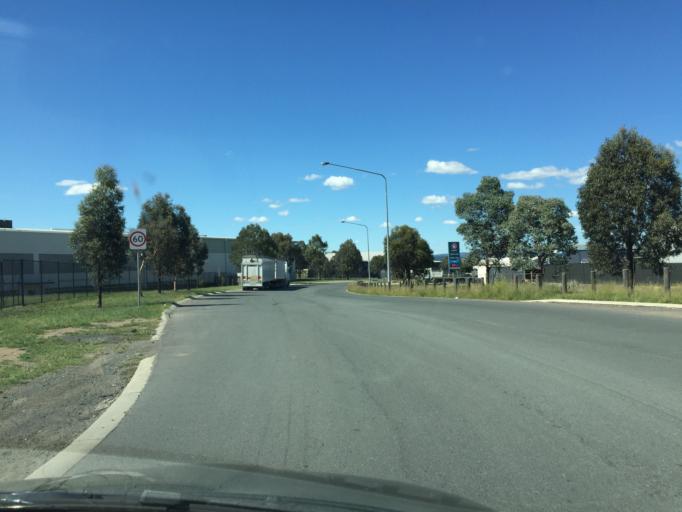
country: AU
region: Australian Capital Territory
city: Macarthur
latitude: -35.3973
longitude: 149.1565
